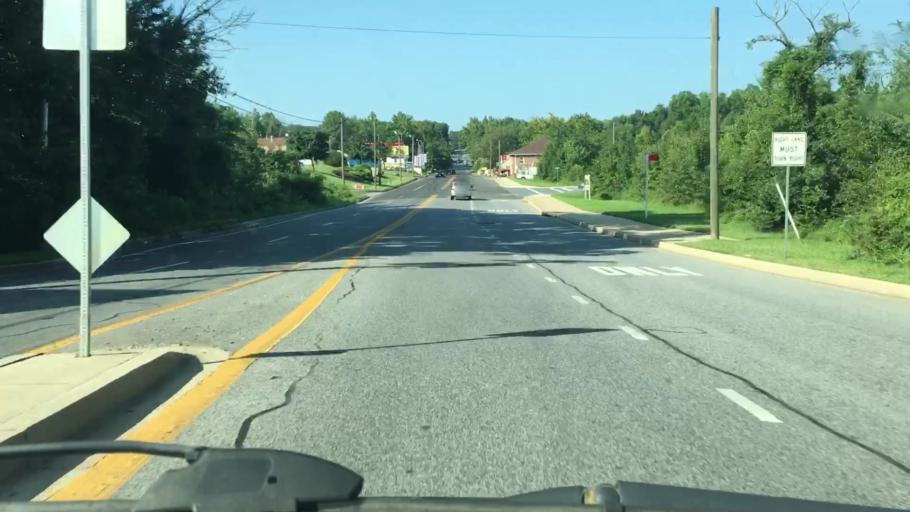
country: US
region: Maryland
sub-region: Prince George's County
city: Glenn Dale
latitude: 38.9869
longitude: -76.8205
